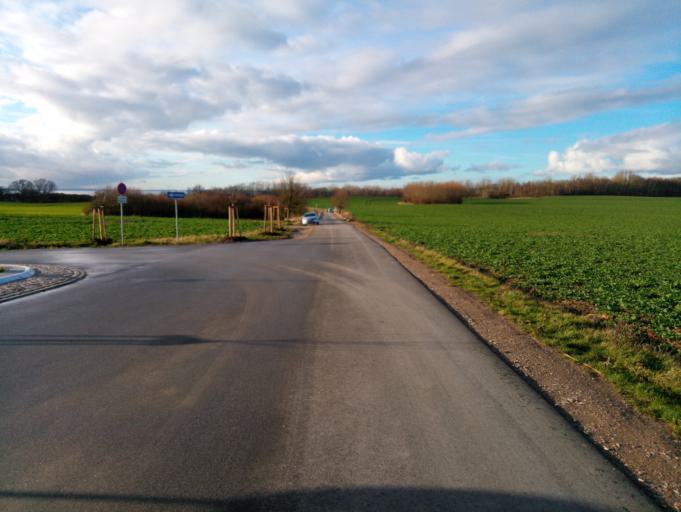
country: DE
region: Mecklenburg-Vorpommern
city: Dassow
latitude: 53.9697
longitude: 10.9619
